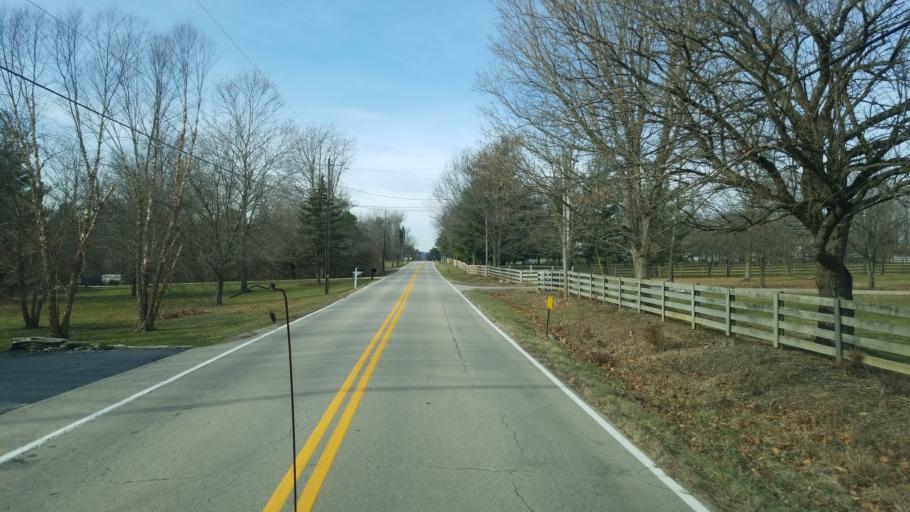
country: US
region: Ohio
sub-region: Warren County
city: Lebanon
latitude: 39.4297
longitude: -84.1535
